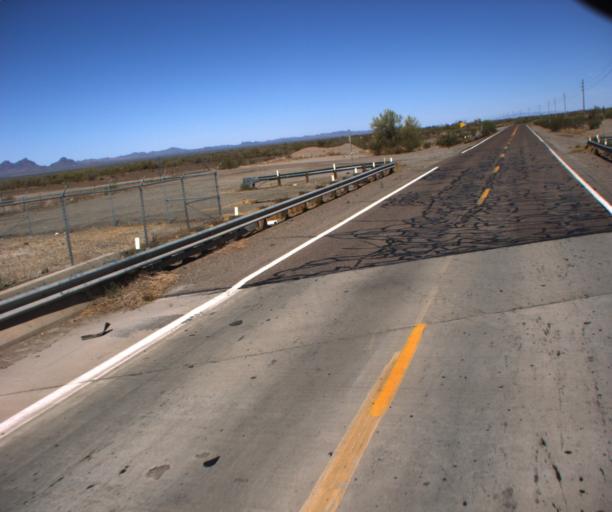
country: US
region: Arizona
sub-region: La Paz County
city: Salome
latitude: 33.7667
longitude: -113.7889
